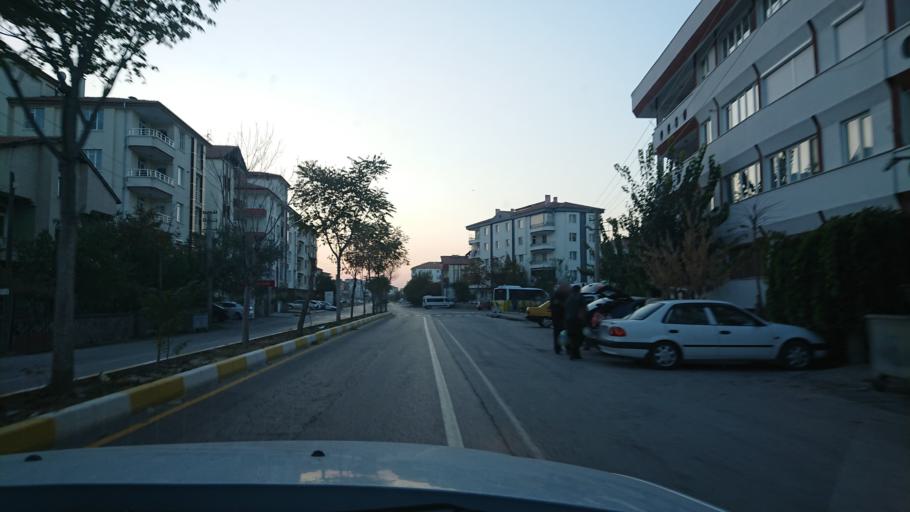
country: TR
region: Aksaray
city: Aksaray
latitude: 38.3604
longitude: 34.0137
